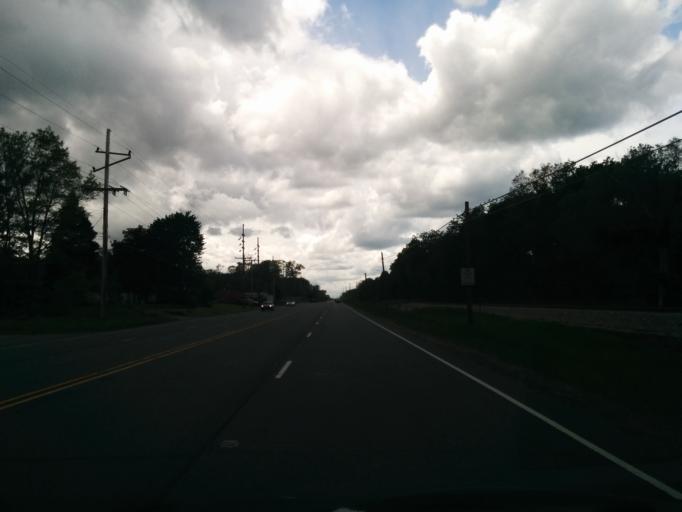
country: US
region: Indiana
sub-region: LaPorte County
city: Long Beach
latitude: 41.7399
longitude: -86.8406
